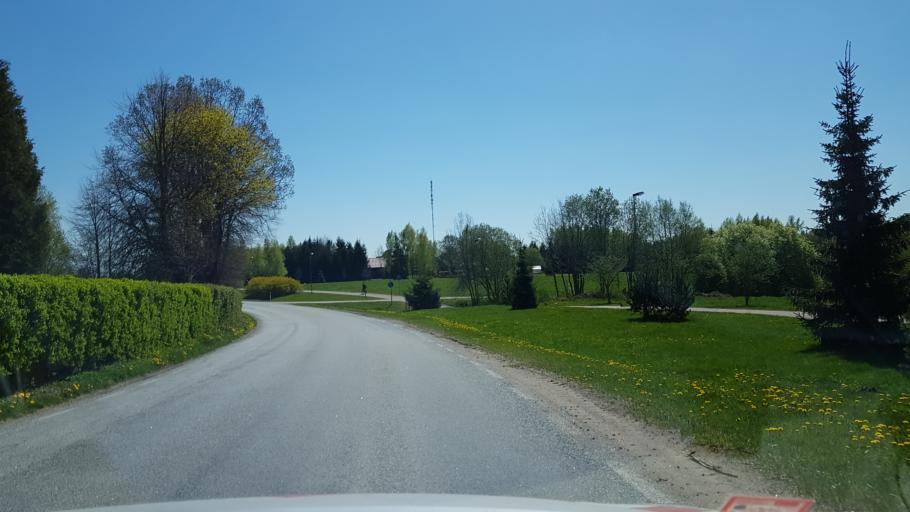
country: EE
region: Vorumaa
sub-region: Voru linn
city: Voru
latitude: 57.9023
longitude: 26.9920
